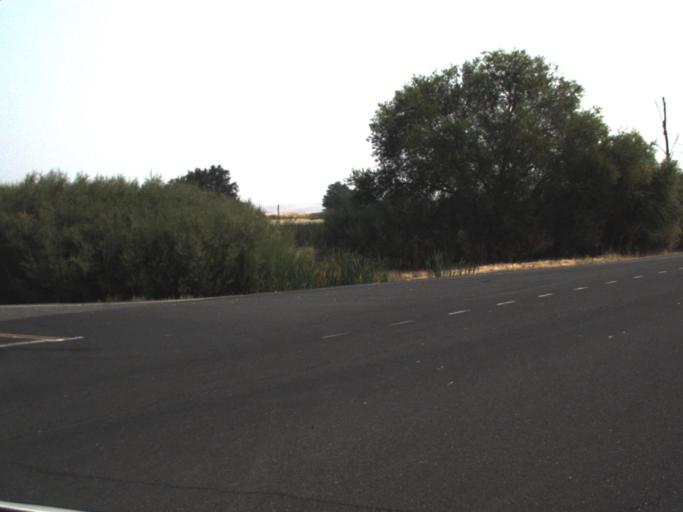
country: US
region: Washington
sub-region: Yakima County
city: Terrace Heights
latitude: 46.5487
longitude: -120.3349
